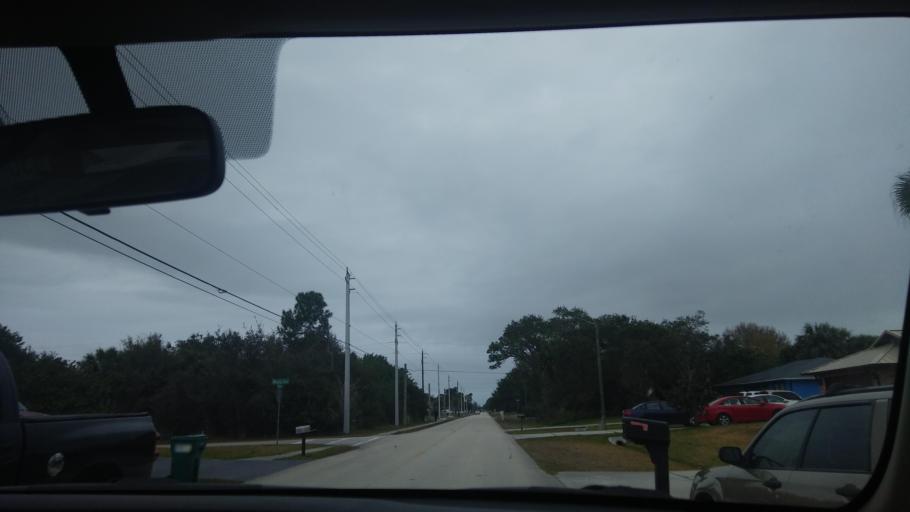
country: US
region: Florida
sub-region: Indian River County
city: Sebastian
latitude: 27.7881
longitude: -80.4948
